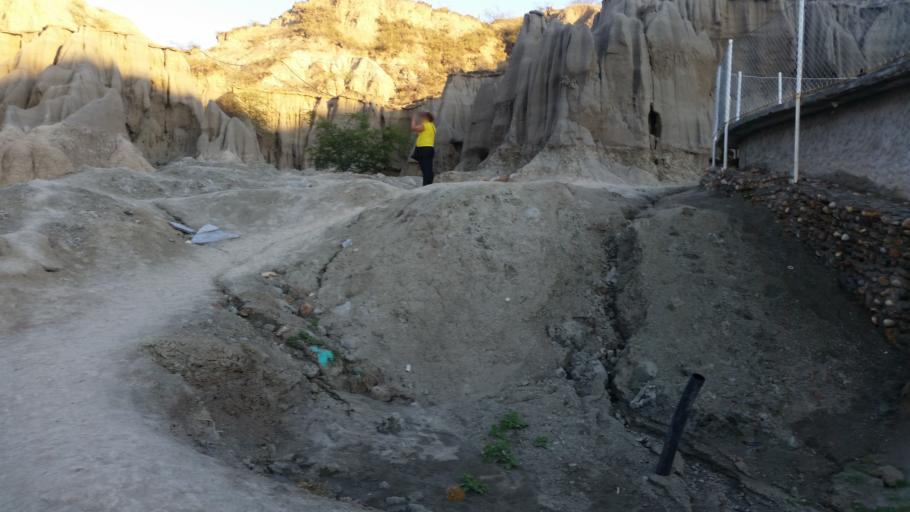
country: CO
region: Huila
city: Villavieja
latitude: 3.2380
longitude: -75.1174
